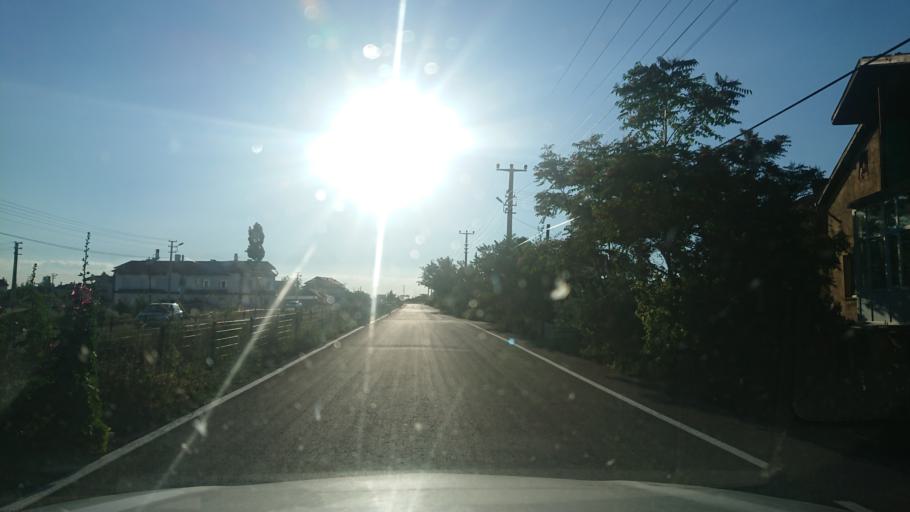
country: TR
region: Aksaray
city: Aksaray
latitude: 38.3904
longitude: 33.9950
